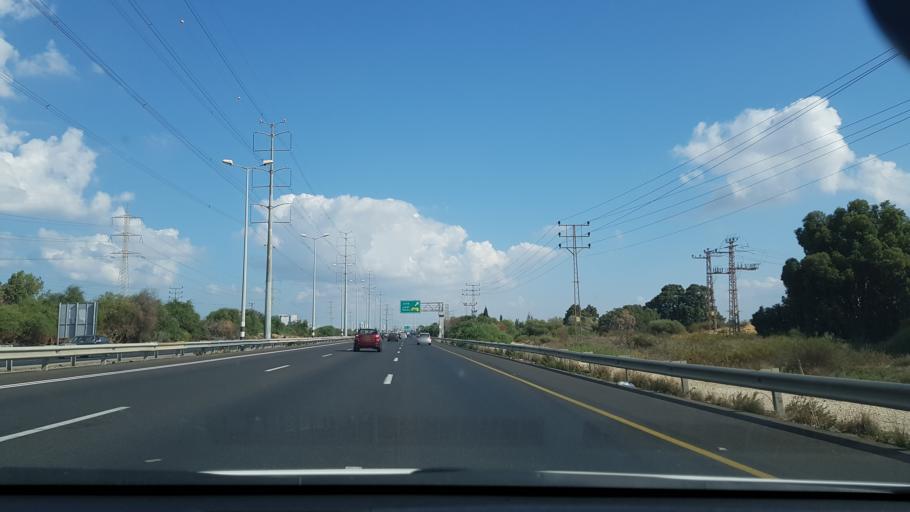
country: IL
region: Central District
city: Rishon LeZiyyon
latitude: 31.9858
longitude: 34.7961
